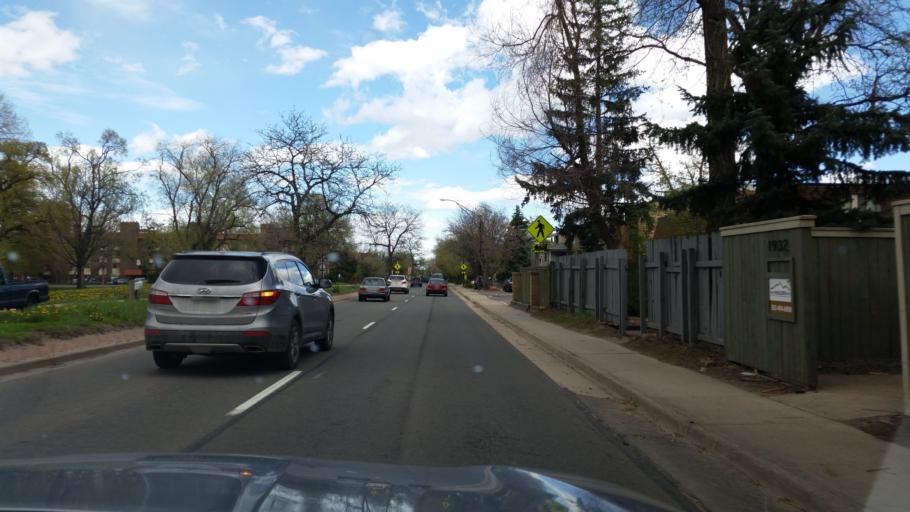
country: US
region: Colorado
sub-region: Boulder County
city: Boulder
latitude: 40.0172
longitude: -105.2695
